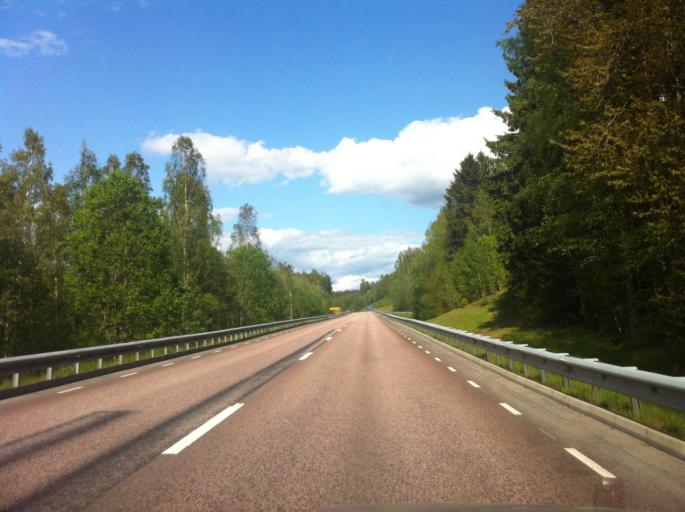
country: SE
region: Vaermland
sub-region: Kristinehamns Kommun
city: Kristinehamn
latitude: 59.3869
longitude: 14.1869
